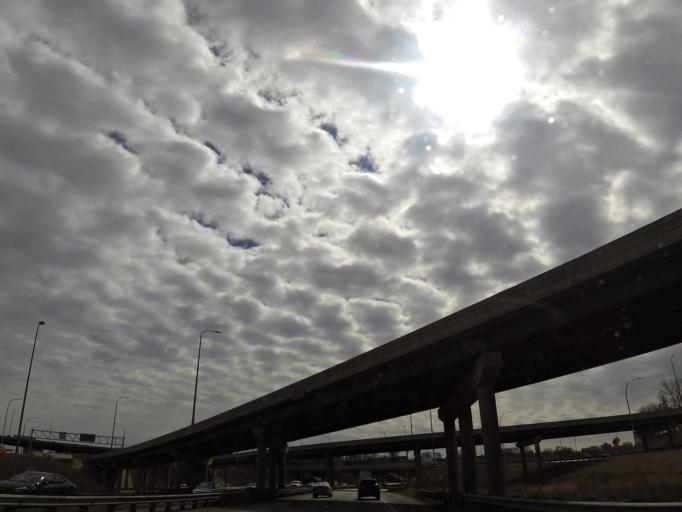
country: US
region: Minnesota
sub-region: Hennepin County
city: Minneapolis
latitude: 44.9688
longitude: -93.2536
